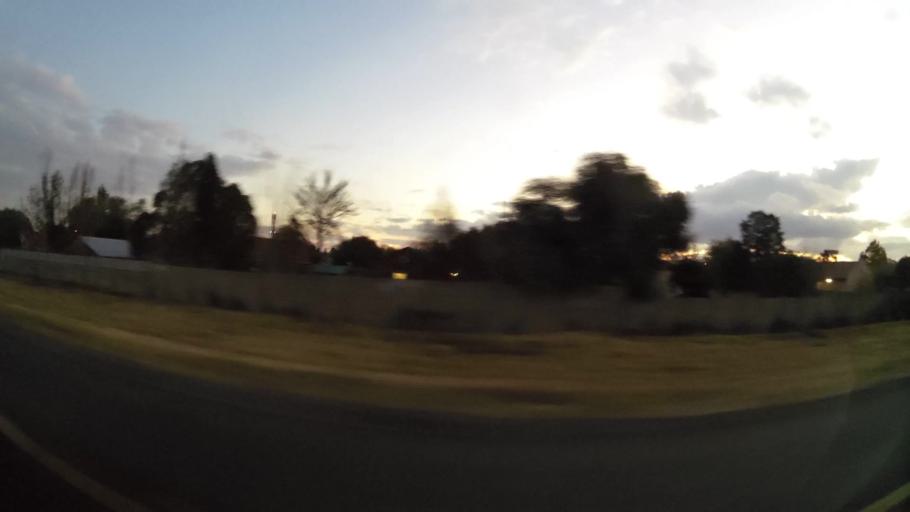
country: ZA
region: Orange Free State
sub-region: Mangaung Metropolitan Municipality
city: Bloemfontein
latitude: -29.1621
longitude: 26.1794
